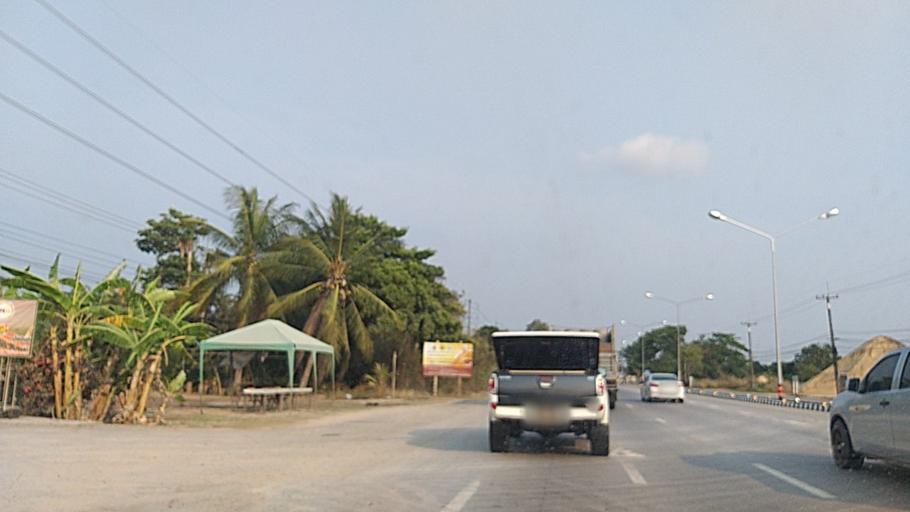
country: TH
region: Chanthaburi
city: Khlung
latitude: 12.4566
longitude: 102.2361
